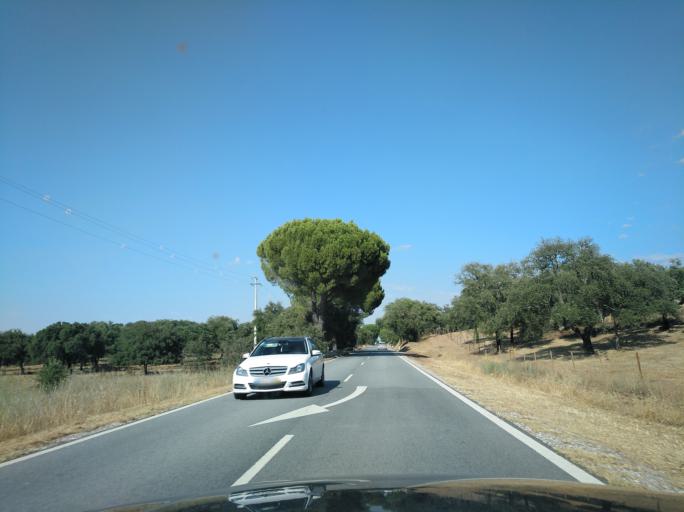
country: ES
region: Andalusia
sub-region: Provincia de Huelva
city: Rosal de la Frontera
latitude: 38.0069
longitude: -7.2813
